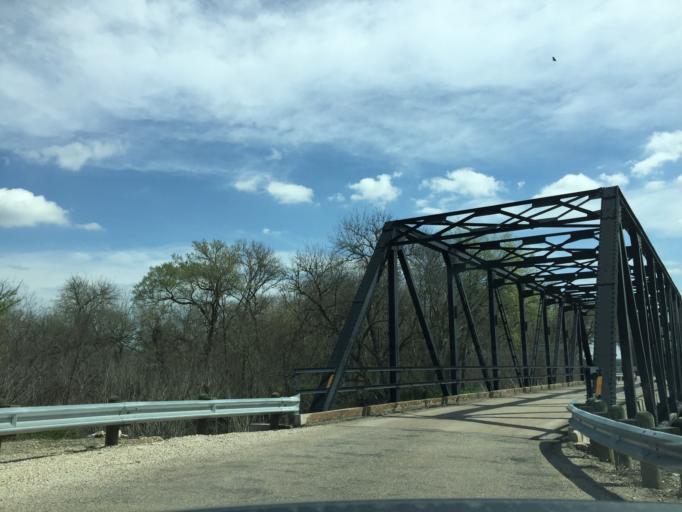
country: US
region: Texas
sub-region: Milam County
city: Thorndale
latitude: 30.5585
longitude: -97.2332
